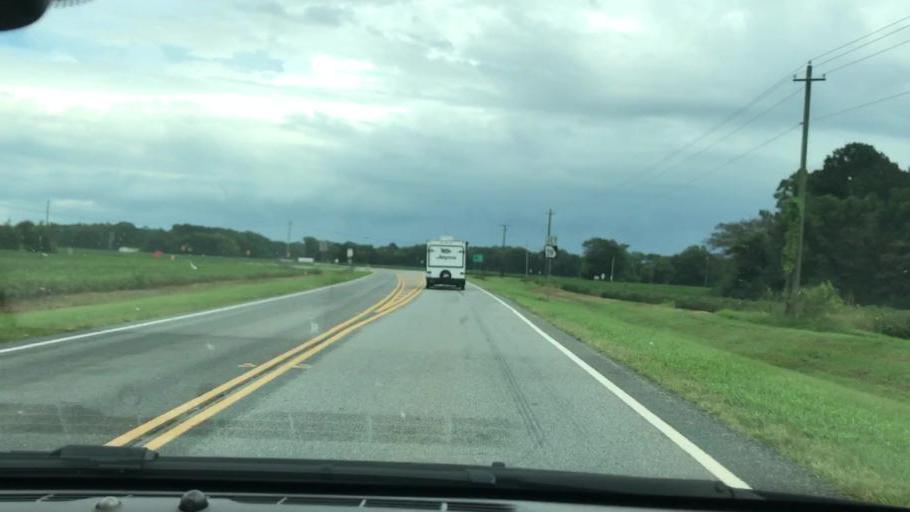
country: US
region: Georgia
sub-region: Early County
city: Blakely
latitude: 31.3897
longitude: -84.9464
